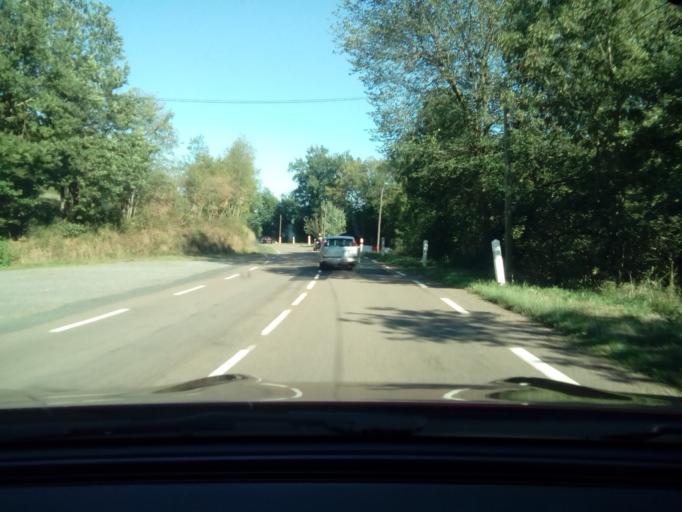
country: FR
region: Rhone-Alpes
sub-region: Departement du Rhone
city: Saint-Verand
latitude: 45.9029
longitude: 4.5353
